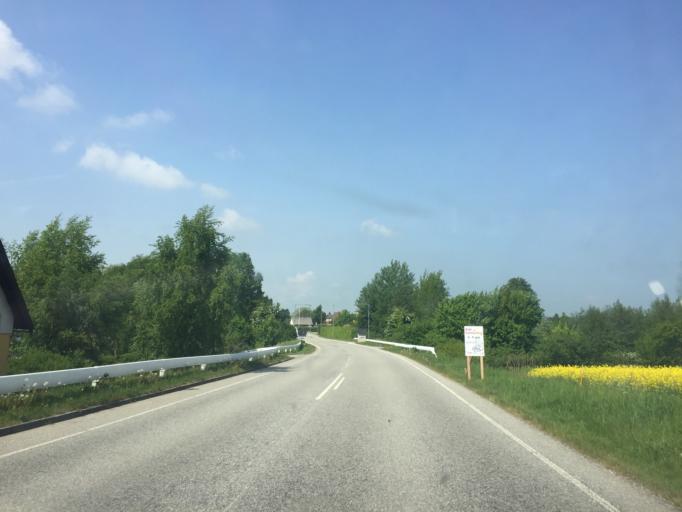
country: DK
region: South Denmark
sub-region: Kolding Kommune
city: Sonder Bjert
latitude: 55.3786
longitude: 9.5831
